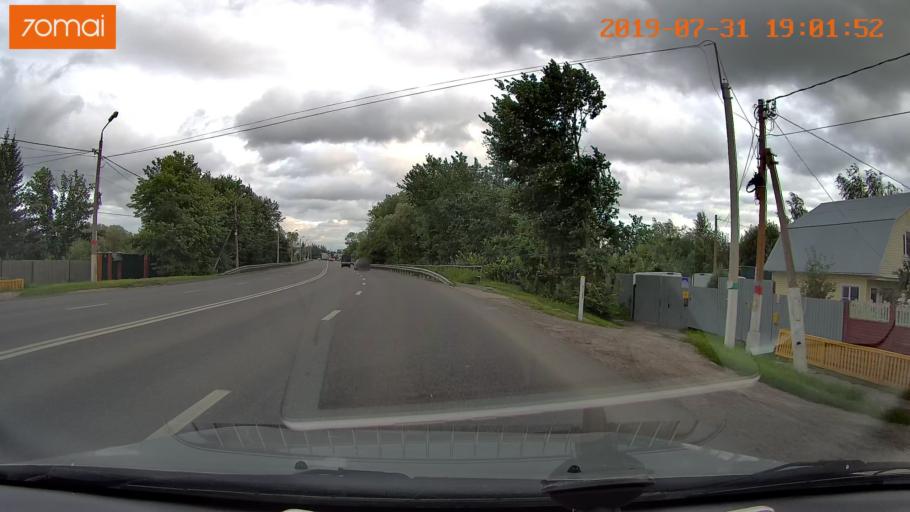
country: RU
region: Moskovskaya
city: Raduzhnyy
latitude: 55.1235
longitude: 38.7296
